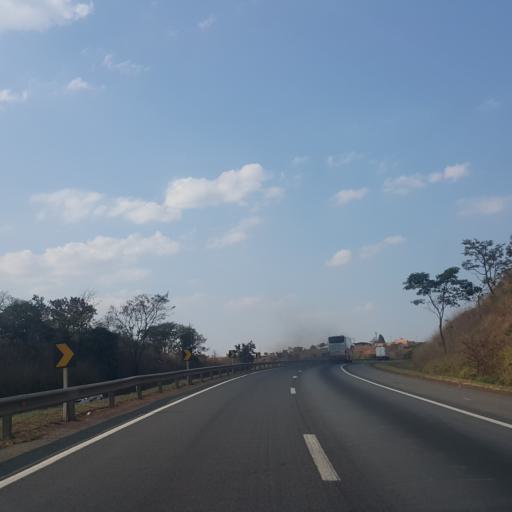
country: BR
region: Goias
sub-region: Abadiania
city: Abadiania
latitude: -16.0985
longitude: -48.5220
